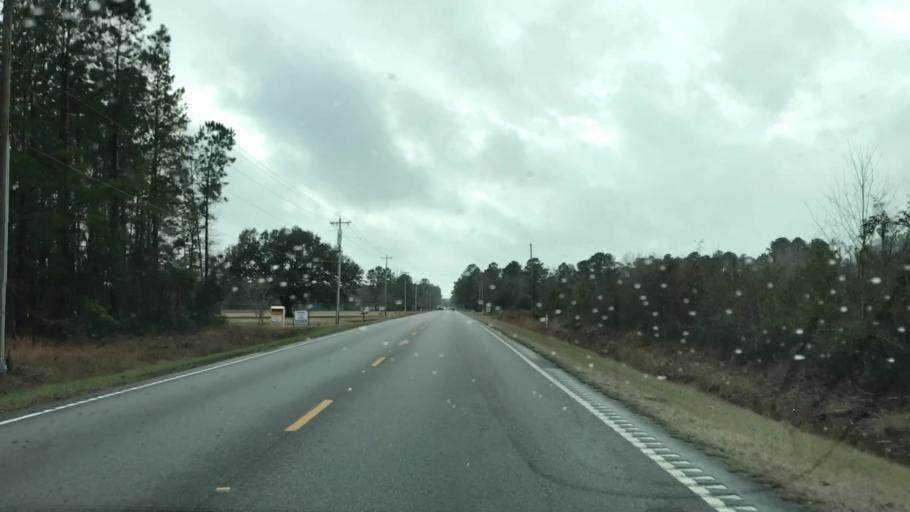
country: US
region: South Carolina
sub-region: Horry County
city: Socastee
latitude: 33.7373
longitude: -79.0812
